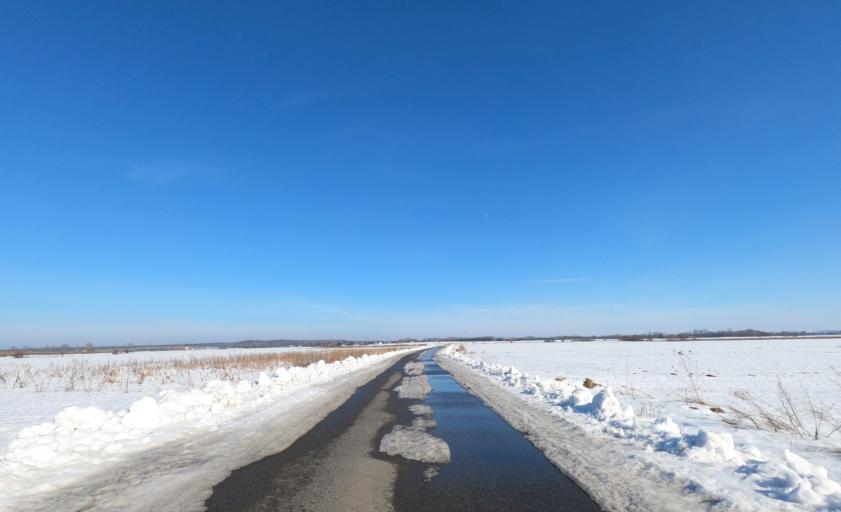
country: PL
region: Subcarpathian Voivodeship
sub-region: Powiat debicki
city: Brzeznica
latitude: 50.0819
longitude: 21.4932
